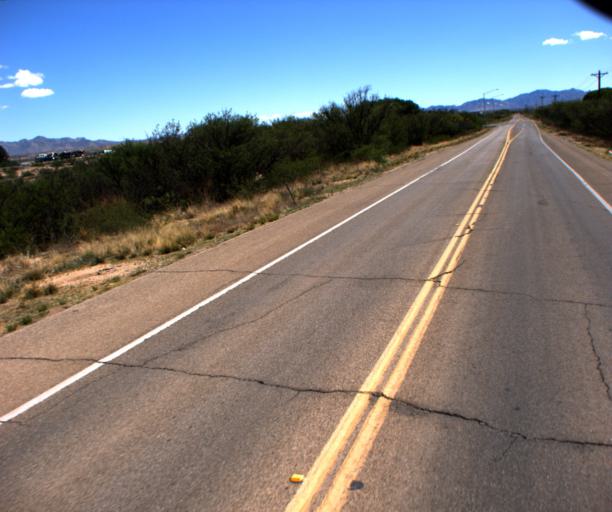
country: US
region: Arizona
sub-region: Cochise County
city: Benson
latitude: 31.9650
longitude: -110.2769
